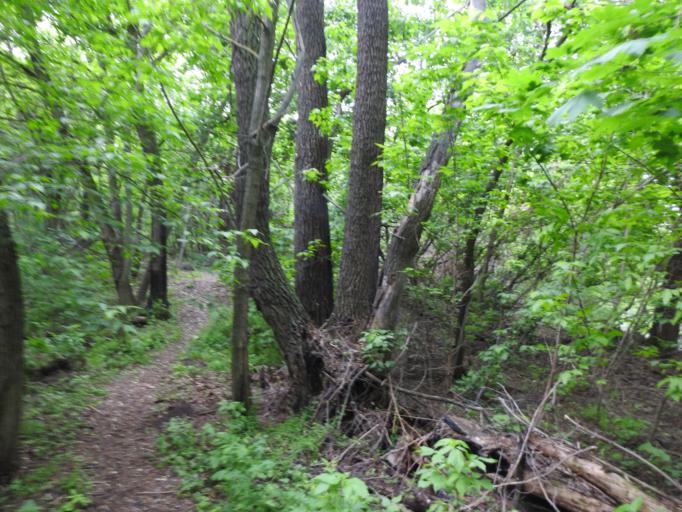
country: RU
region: Saratov
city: Engel's
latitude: 51.4681
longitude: 46.0756
